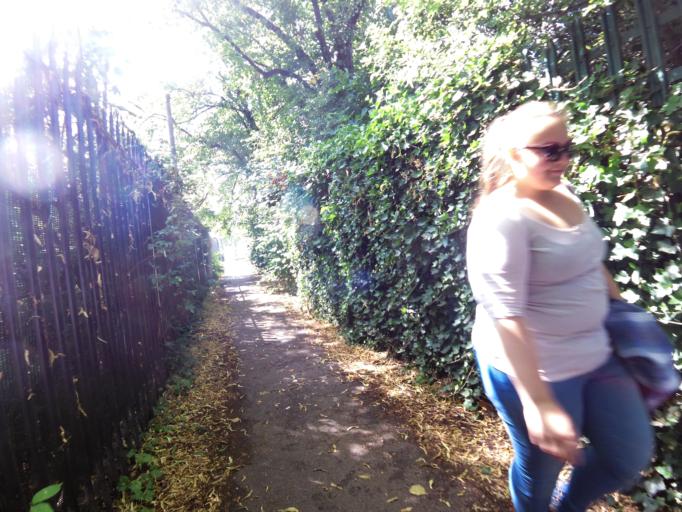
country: GB
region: England
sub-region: Greater London
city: Hackney
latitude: 51.5732
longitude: -0.0575
